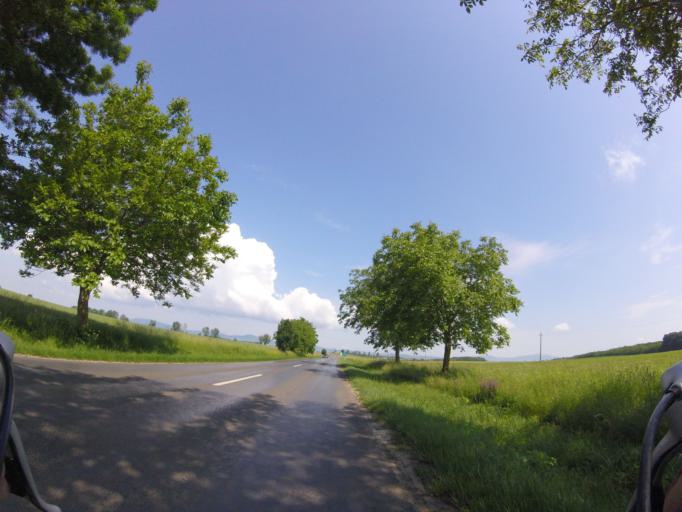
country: HU
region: Baranya
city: Kozarmisleny
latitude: 46.0131
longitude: 18.3058
